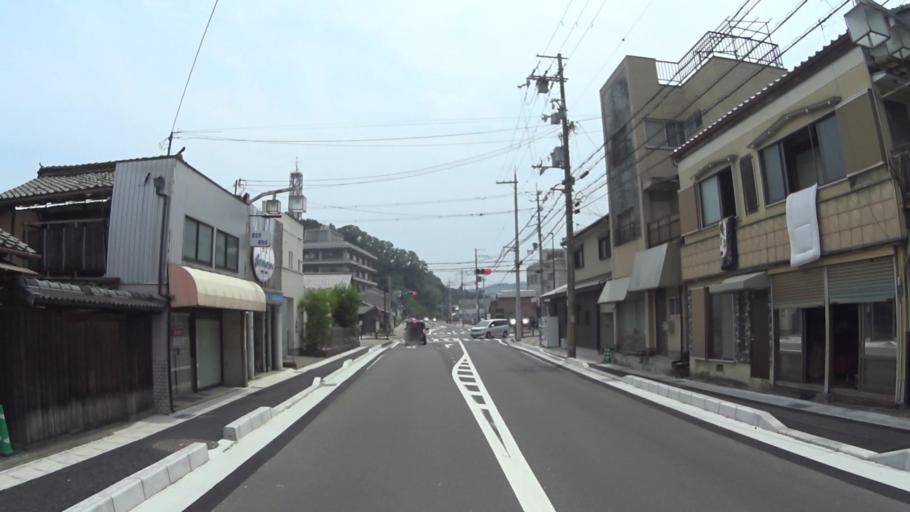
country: JP
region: Kyoto
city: Kameoka
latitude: 35.1114
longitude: 135.4752
